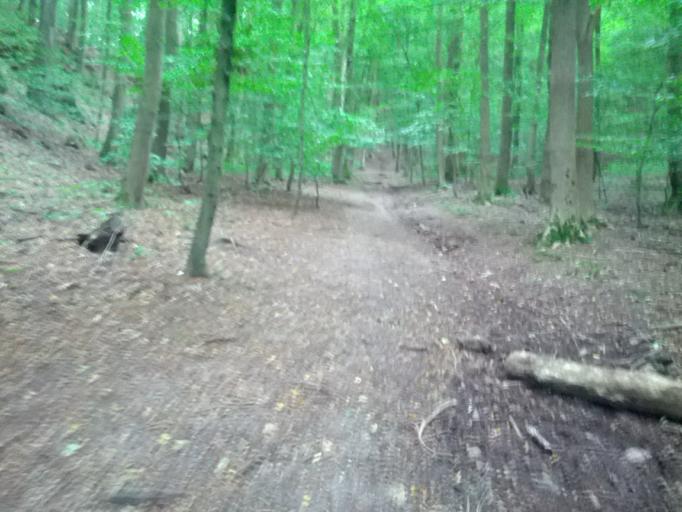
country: DE
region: Thuringia
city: Eisenach
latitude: 50.9634
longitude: 10.3124
